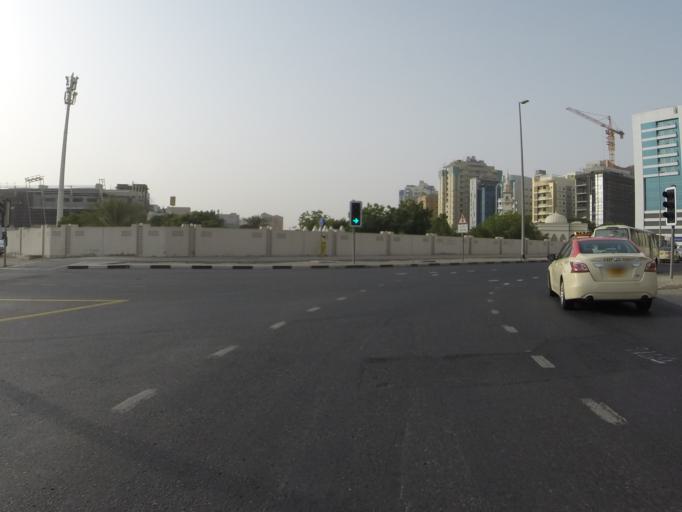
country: AE
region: Dubai
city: Dubai
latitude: 25.1196
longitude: 55.2044
